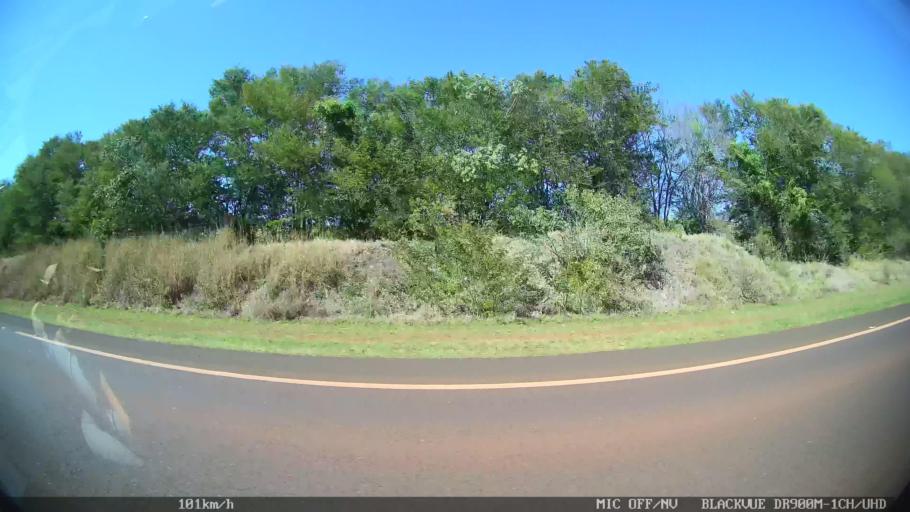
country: BR
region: Sao Paulo
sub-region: Franca
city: Franca
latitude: -20.6489
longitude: -47.4838
